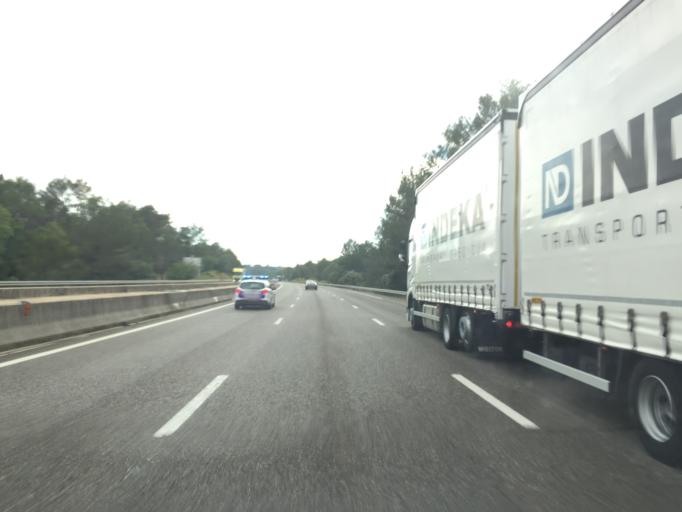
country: FR
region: Provence-Alpes-Cote d'Azur
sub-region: Departement du Var
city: Bras
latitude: 43.4251
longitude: 5.9754
